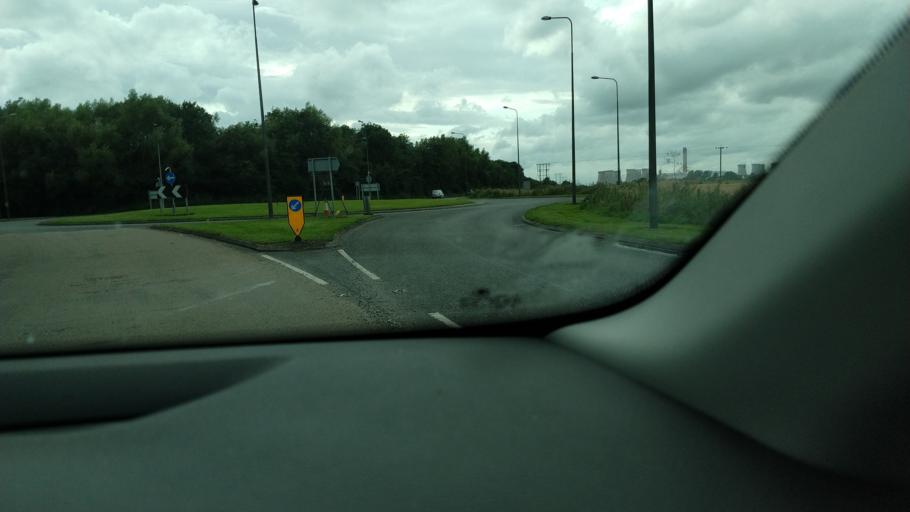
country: GB
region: England
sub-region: East Riding of Yorkshire
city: Rawcliffe
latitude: 53.7063
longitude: -0.9348
